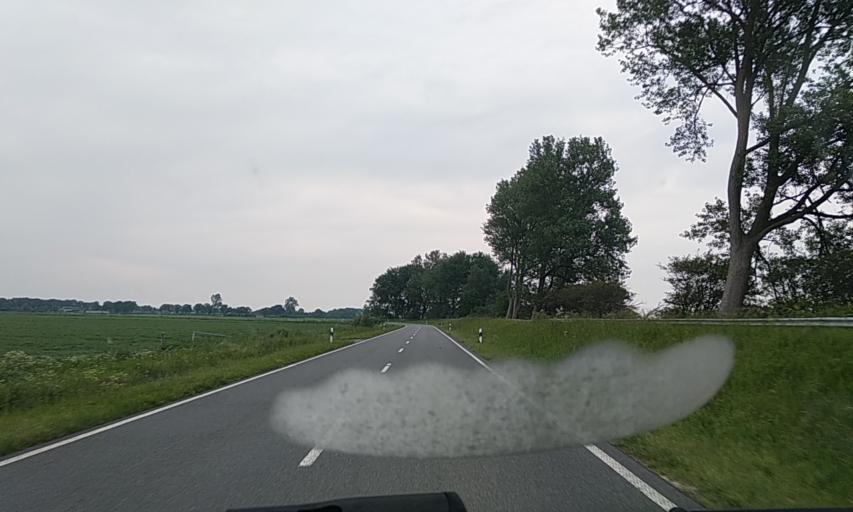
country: DE
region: Schleswig-Holstein
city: Meggerdorf
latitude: 54.3337
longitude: 9.3994
